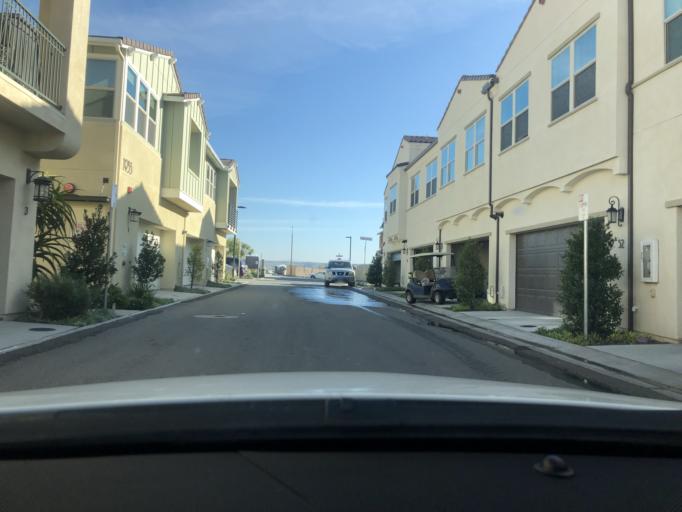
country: US
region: California
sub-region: San Diego County
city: Bonita
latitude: 32.5993
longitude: -117.0010
